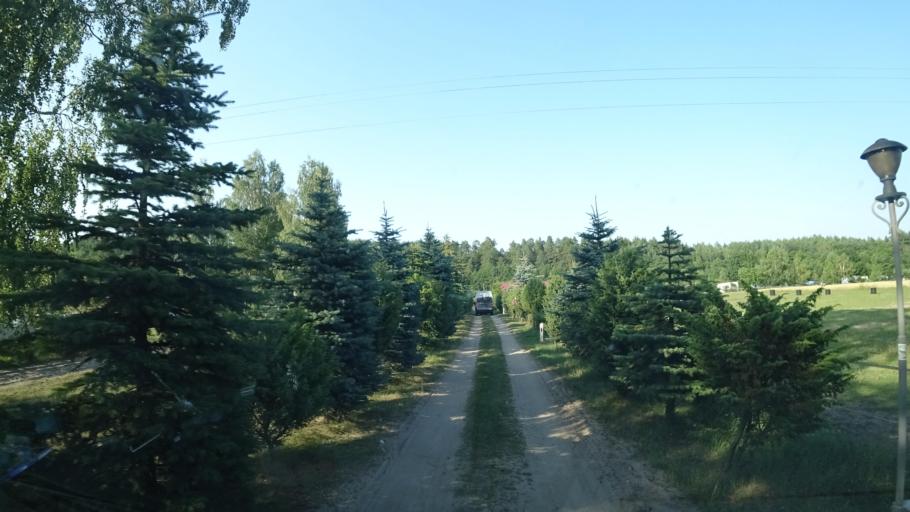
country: PL
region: Pomeranian Voivodeship
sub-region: Powiat chojnicki
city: Brusy
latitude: 53.8687
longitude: 17.5461
